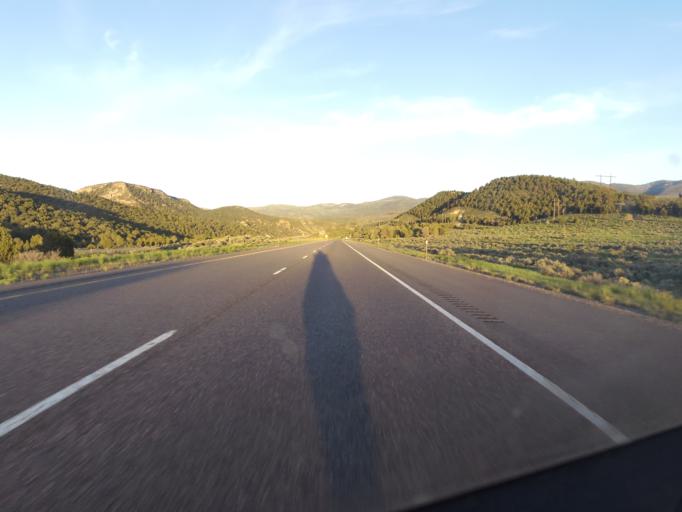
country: US
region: Utah
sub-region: Sevier County
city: Monroe
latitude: 38.5689
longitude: -112.4481
